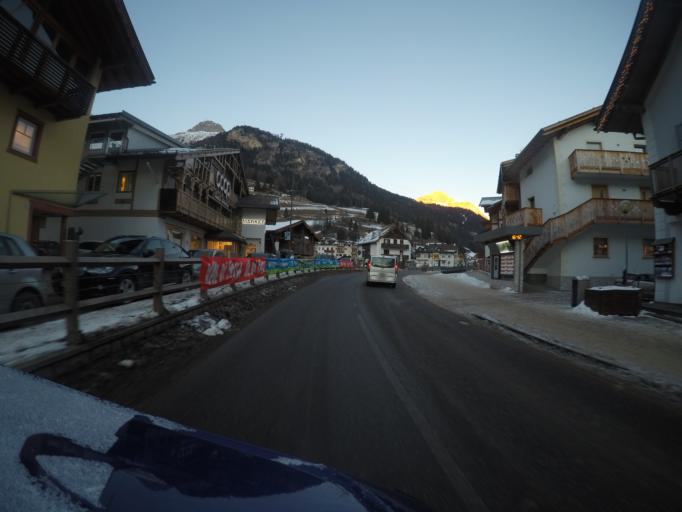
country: IT
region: Trentino-Alto Adige
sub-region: Provincia di Trento
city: Campitello di Fassa
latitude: 46.4760
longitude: 11.7402
